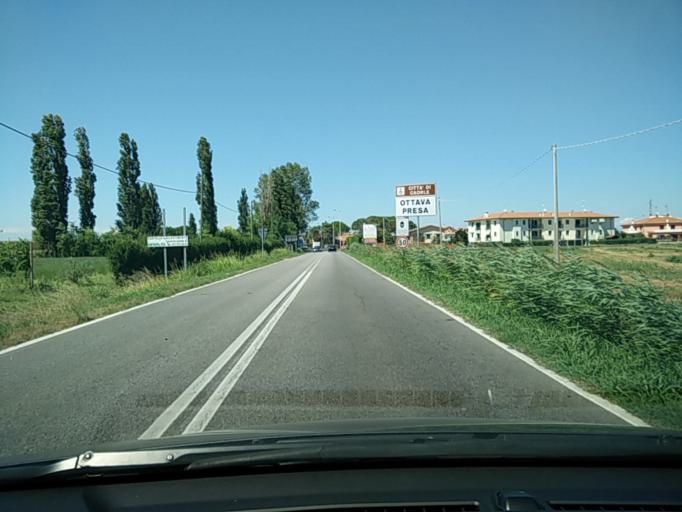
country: IT
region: Veneto
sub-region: Provincia di Venezia
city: La Salute di Livenza
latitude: 45.6432
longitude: 12.8434
